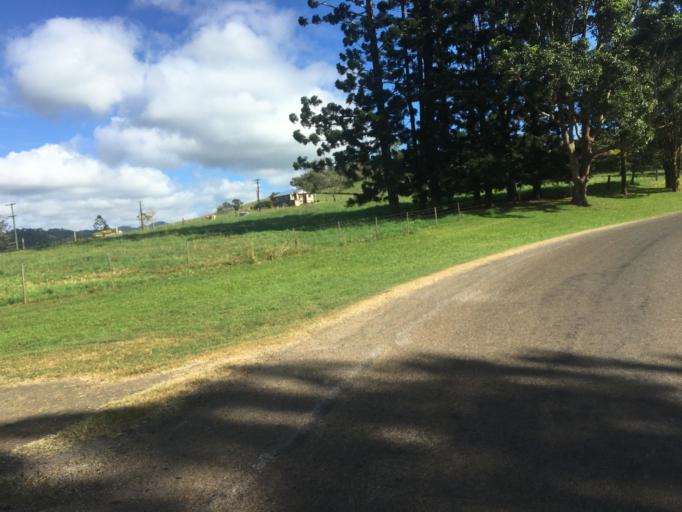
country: AU
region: Queensland
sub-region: Tablelands
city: Ravenshoe
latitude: -17.5242
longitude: 145.6106
